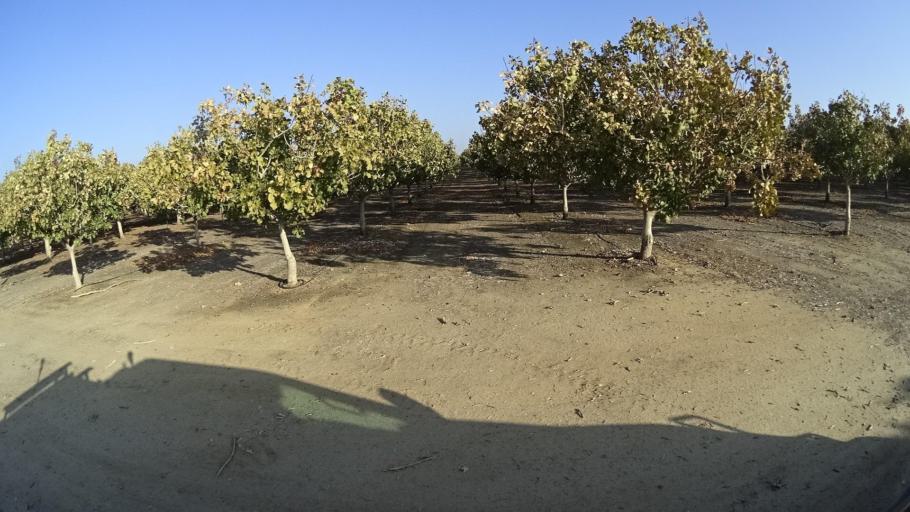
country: US
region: California
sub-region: Tulare County
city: Richgrove
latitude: 35.7763
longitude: -119.0873
